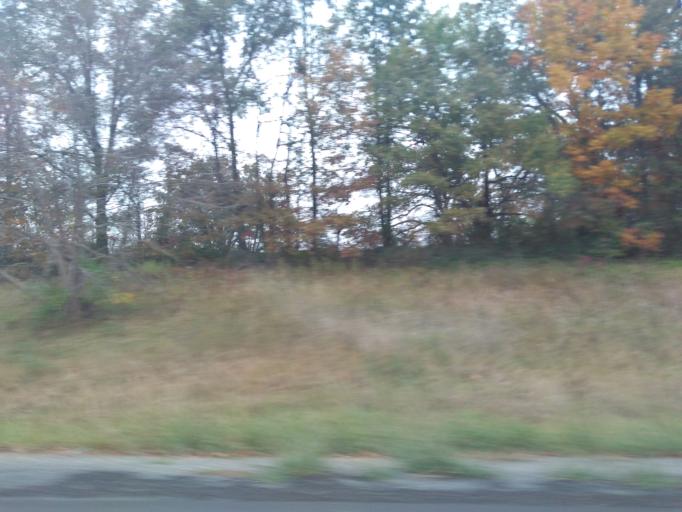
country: US
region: Illinois
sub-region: Madison County
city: Highland
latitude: 38.7866
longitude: -89.6538
